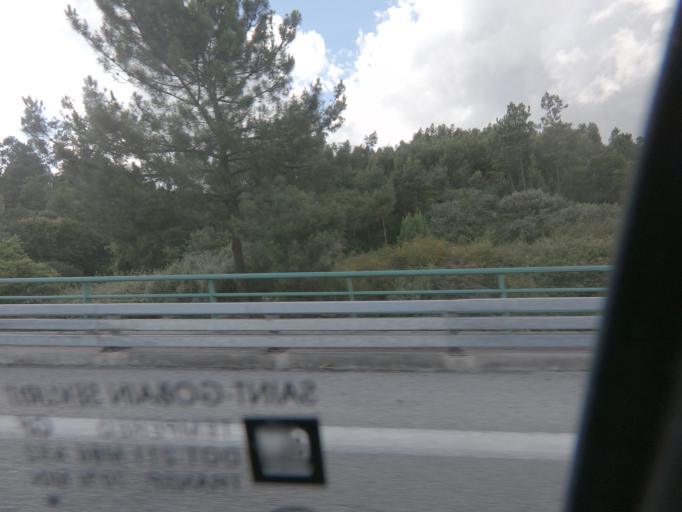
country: PT
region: Porto
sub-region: Marco de Canaveses
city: Marco de Canavezes
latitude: 41.2330
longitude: -8.1249
